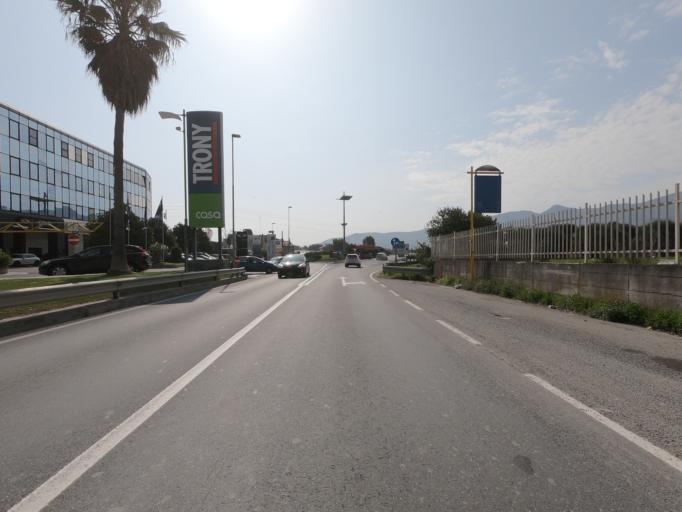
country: IT
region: Liguria
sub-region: Provincia di Savona
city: San Fedele-Lusignano
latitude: 44.0692
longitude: 8.1697
